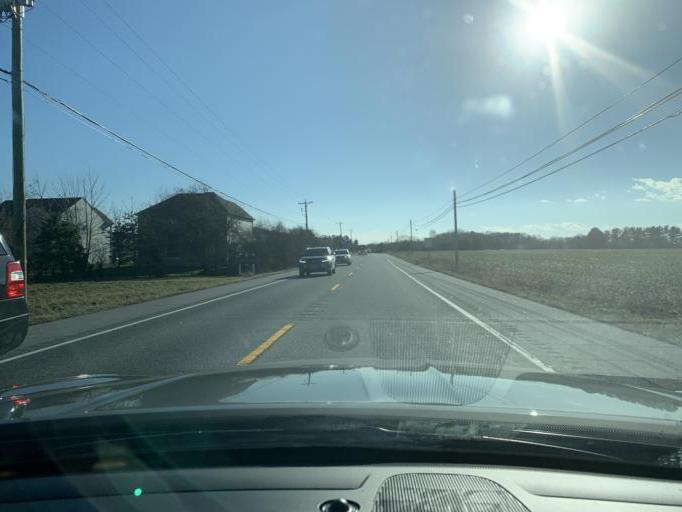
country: US
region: Maryland
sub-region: Queen Anne's County
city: Centreville
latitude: 39.0654
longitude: -76.0507
